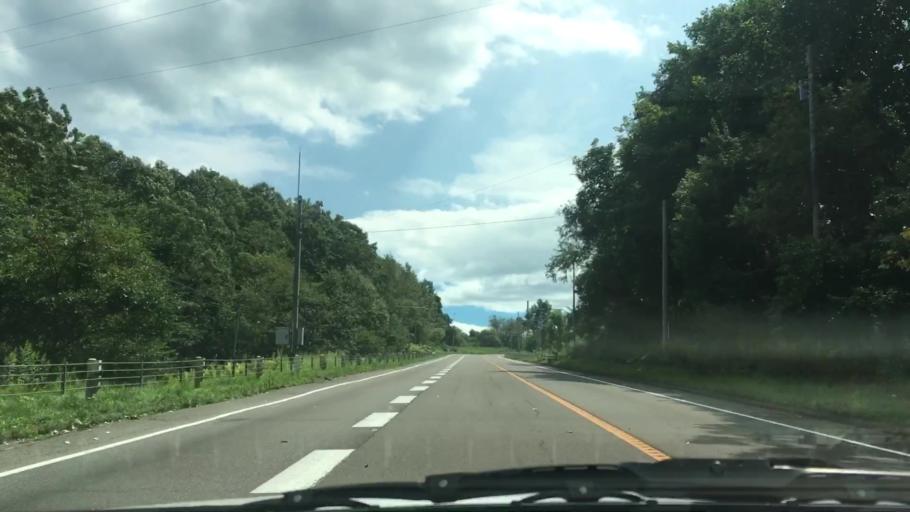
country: JP
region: Hokkaido
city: Otofuke
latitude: 43.2800
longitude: 143.4065
